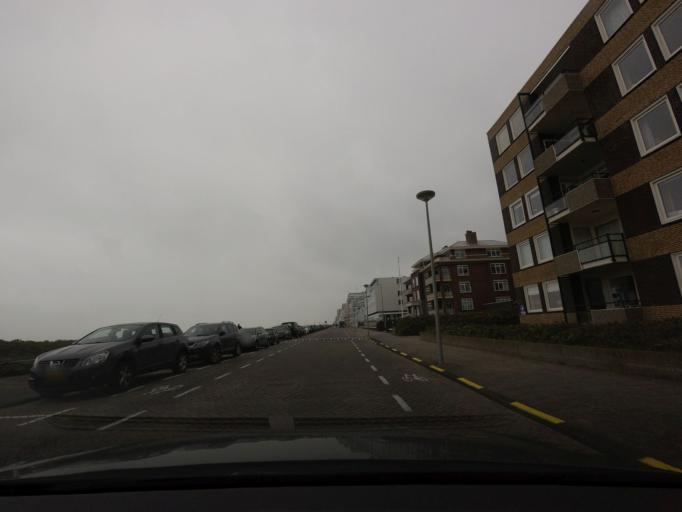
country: NL
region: South Holland
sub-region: Gemeente Noordwijk
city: Noordwijk-Binnen
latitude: 52.2383
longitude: 4.4249
